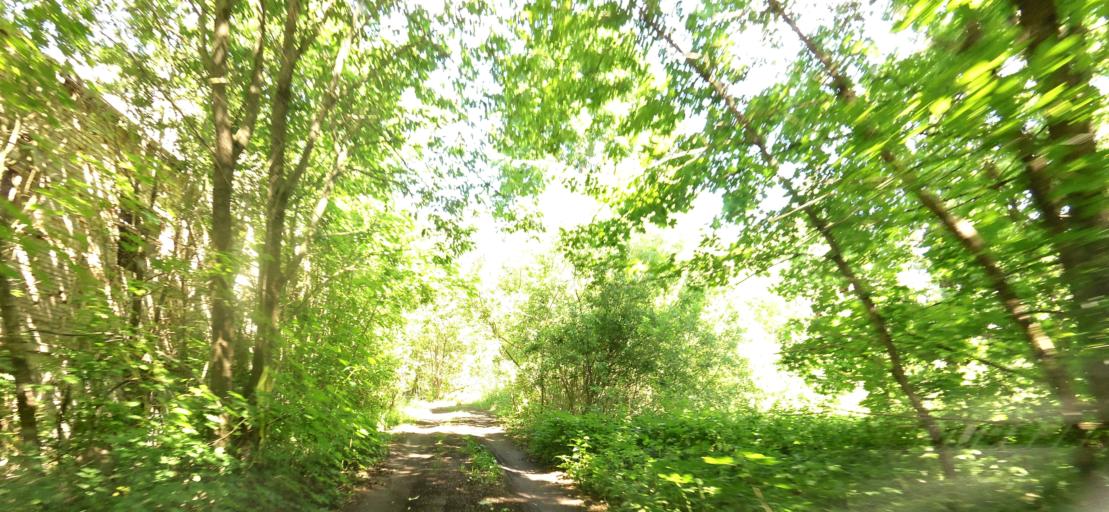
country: LT
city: Nemencine
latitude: 54.8727
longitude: 25.5408
